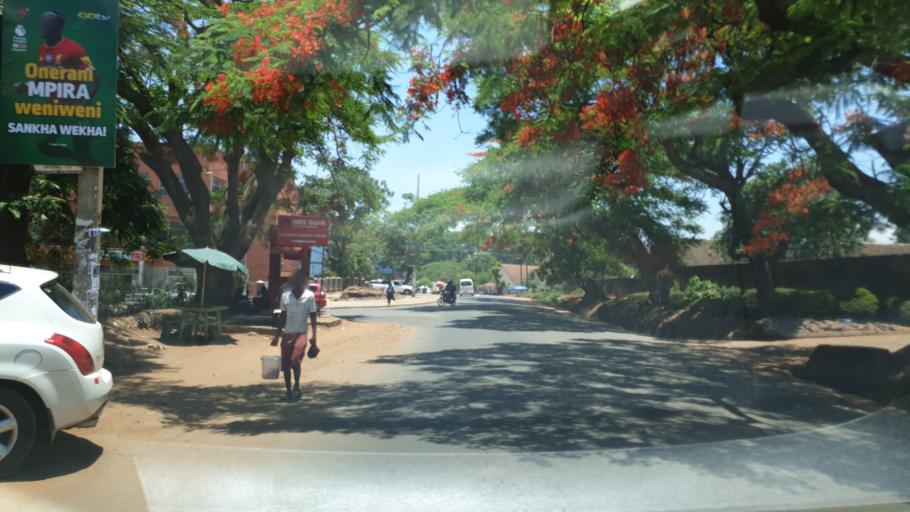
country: MW
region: Central Region
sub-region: Lilongwe District
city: Lilongwe
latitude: -13.9879
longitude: 33.7655
